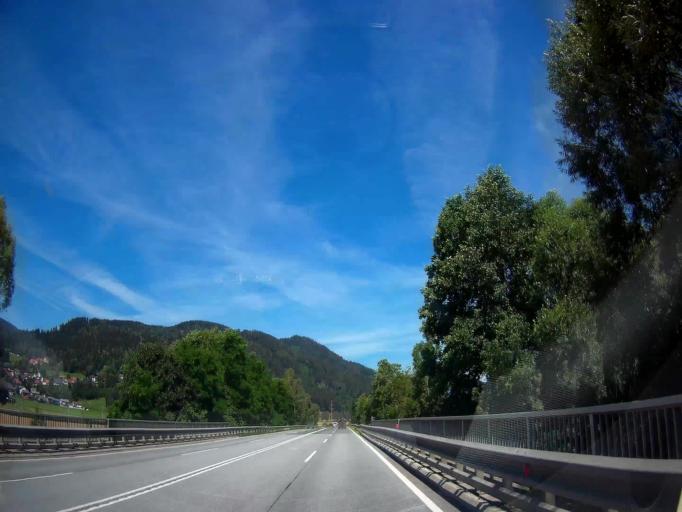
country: AT
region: Carinthia
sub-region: Politischer Bezirk Sankt Veit an der Glan
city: Micheldorf
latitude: 46.9164
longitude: 14.4352
